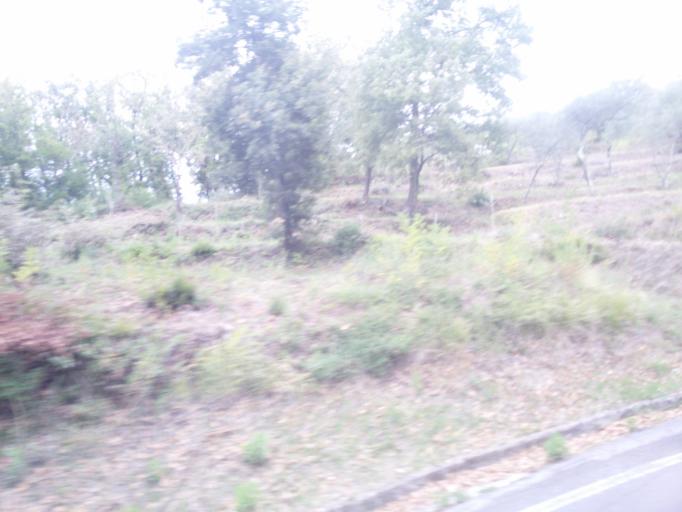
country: IT
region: Liguria
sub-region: Provincia di La Spezia
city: Santo Stefano di Magra
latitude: 44.1593
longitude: 9.9297
